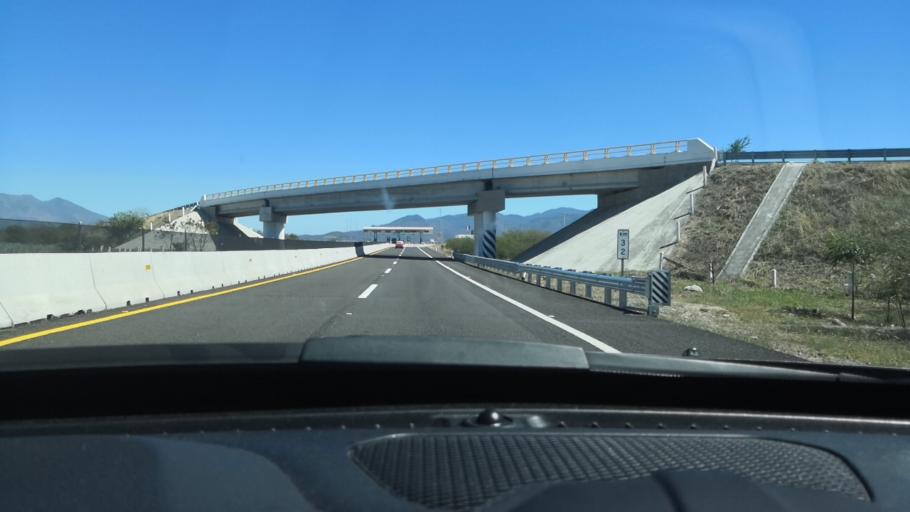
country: MX
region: Nayarit
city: San Pedro Lagunillas
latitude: 21.0966
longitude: -104.7613
